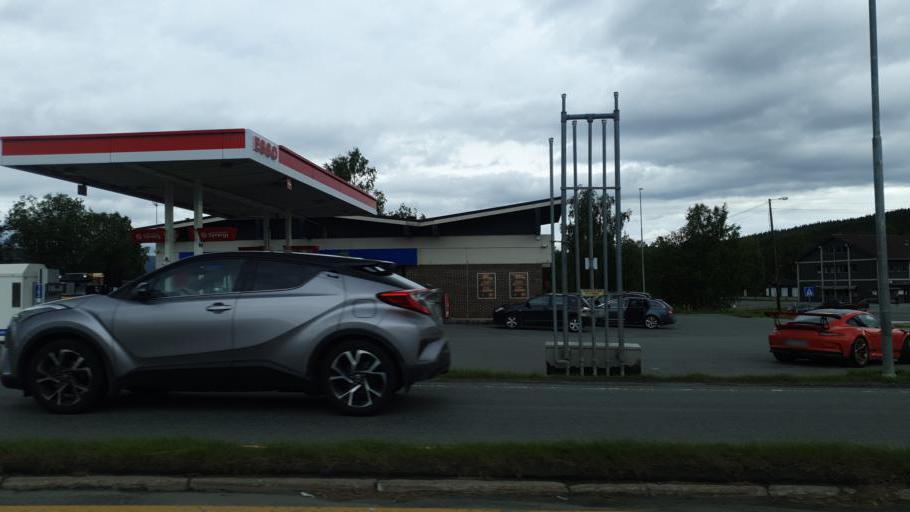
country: NO
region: Sor-Trondelag
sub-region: Rennebu
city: Berkak
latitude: 62.8277
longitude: 10.0091
